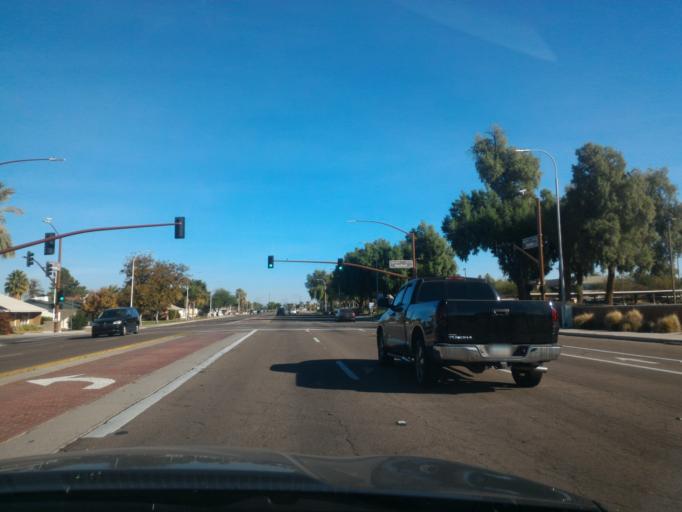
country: US
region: Arizona
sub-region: Maricopa County
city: Chandler
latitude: 33.3060
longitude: -111.8508
